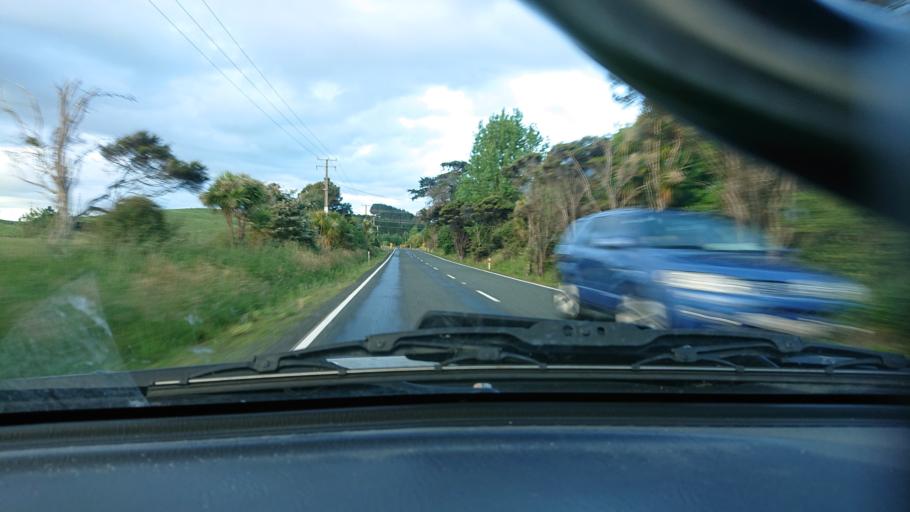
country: NZ
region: Auckland
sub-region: Auckland
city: Parakai
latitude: -36.4862
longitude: 174.4493
